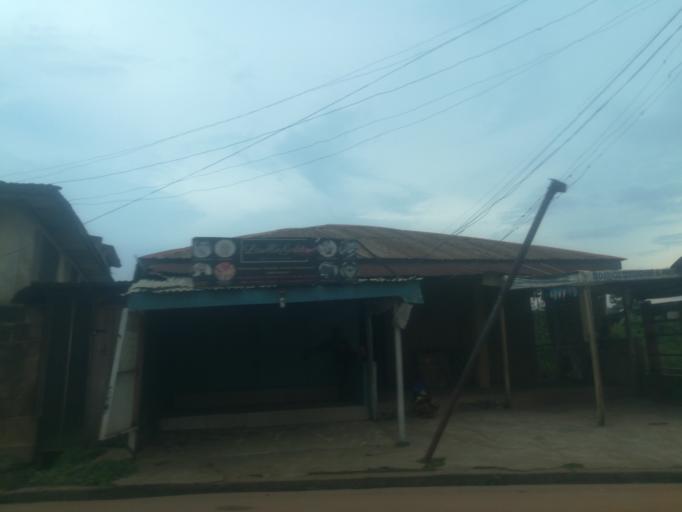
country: NG
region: Oyo
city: Ibadan
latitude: 7.4434
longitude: 3.9118
